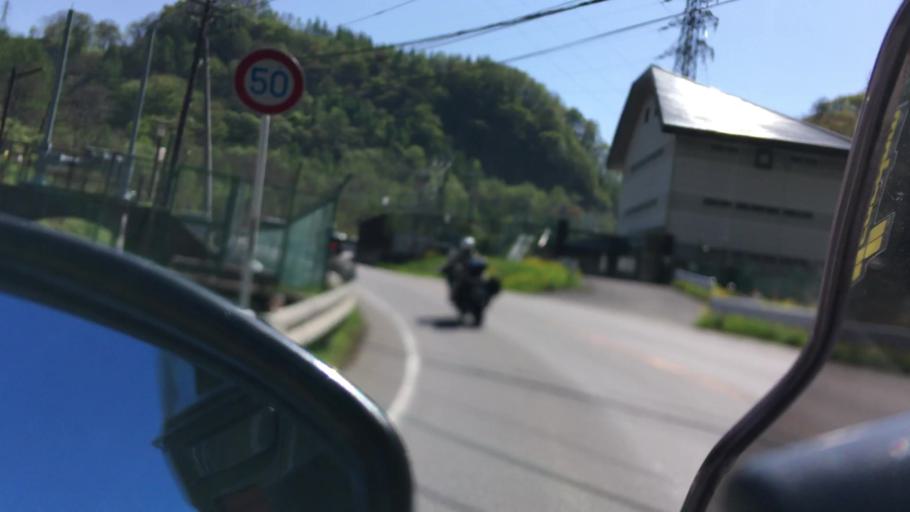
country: JP
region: Nagano
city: Komoro
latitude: 36.4863
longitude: 138.4850
